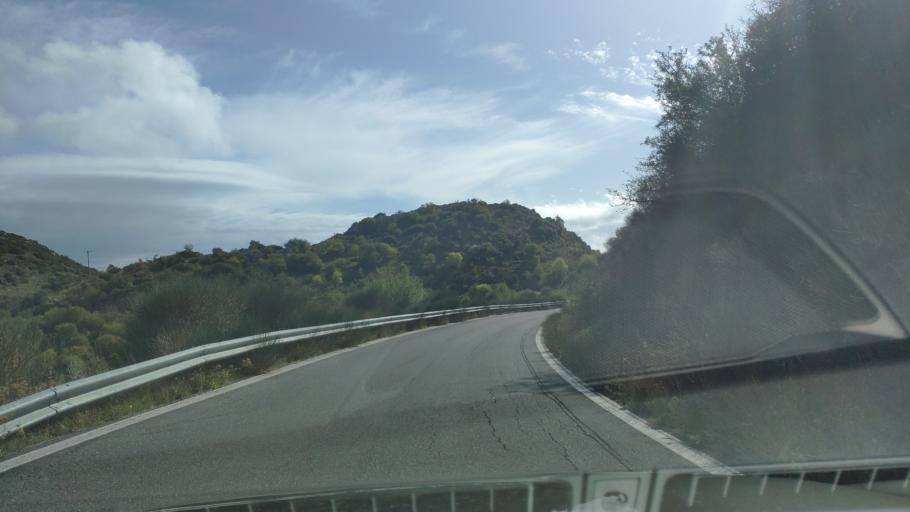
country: GR
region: Peloponnese
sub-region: Nomos Arkadias
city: Dimitsana
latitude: 37.5809
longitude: 22.0172
